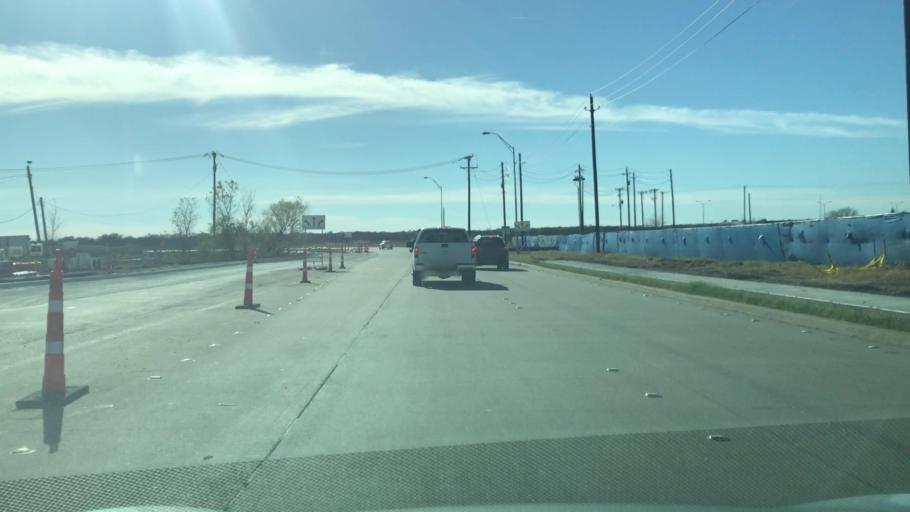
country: US
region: Texas
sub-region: Tarrant County
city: Mansfield
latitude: 32.5632
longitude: -97.0861
